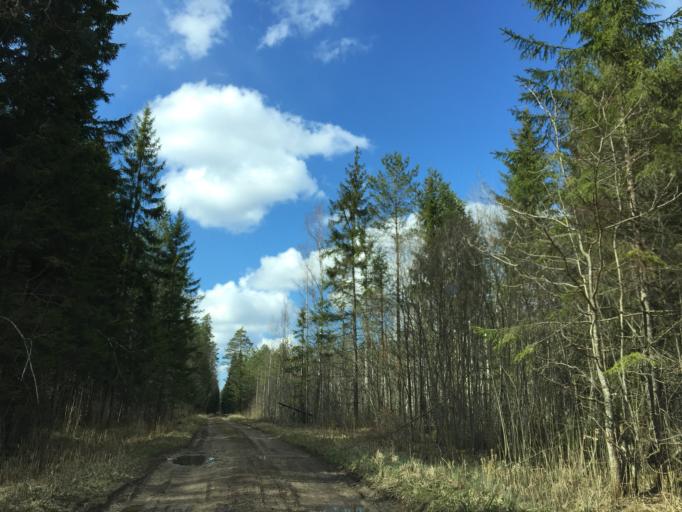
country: LV
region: Garkalne
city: Garkalne
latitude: 56.9481
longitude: 24.4796
